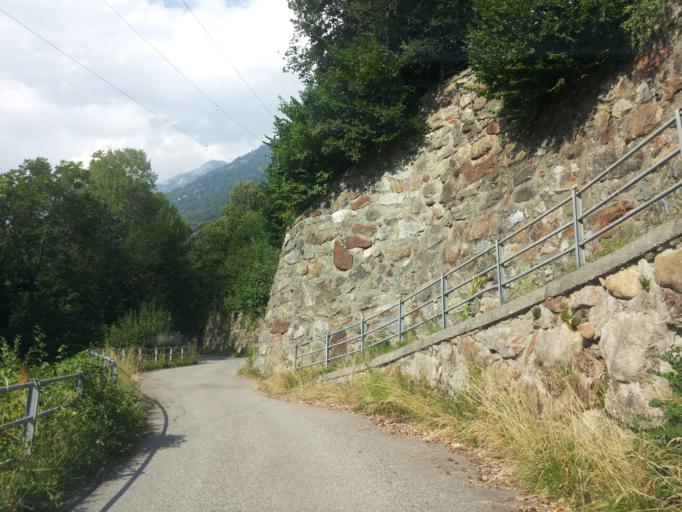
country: IT
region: Aosta Valley
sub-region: Valle d'Aosta
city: Fontainemore
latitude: 45.6457
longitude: 7.8626
